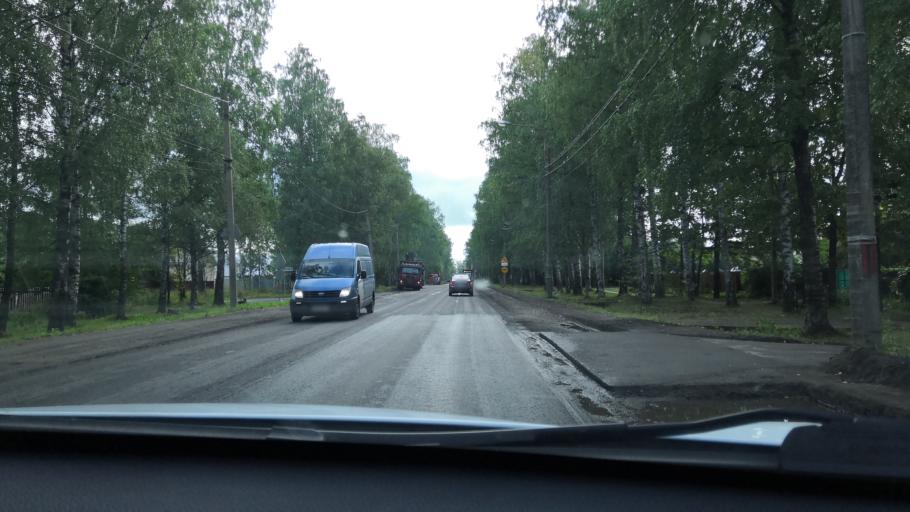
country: RU
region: St.-Petersburg
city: Tyarlevo
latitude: 59.7123
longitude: 30.4430
